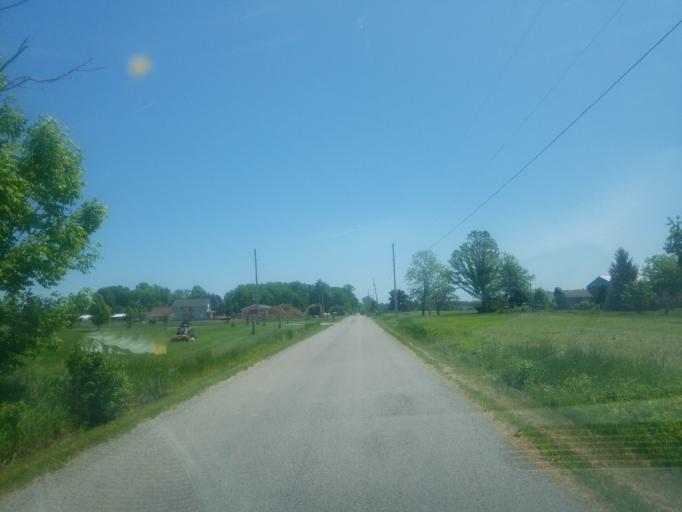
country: US
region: Ohio
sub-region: Huron County
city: New London
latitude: 41.1379
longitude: -82.3527
